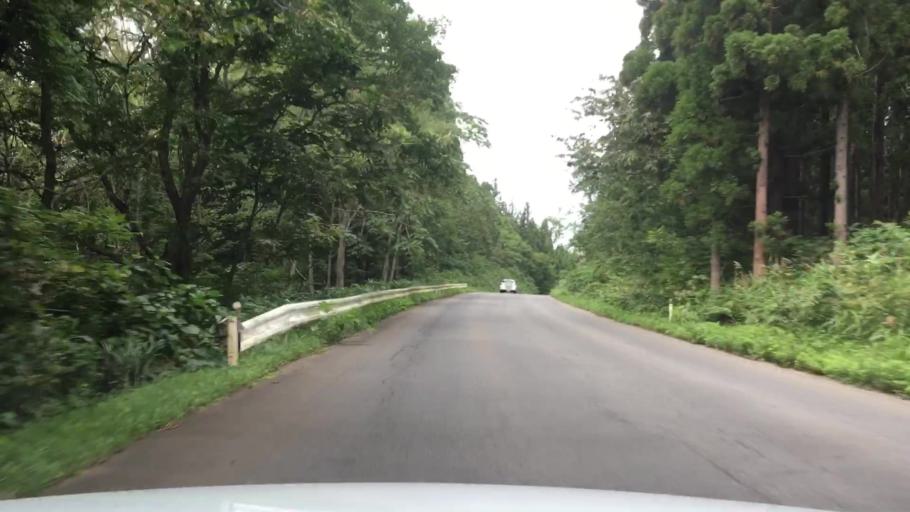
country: JP
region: Aomori
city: Shimokizukuri
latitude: 40.7155
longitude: 140.2613
